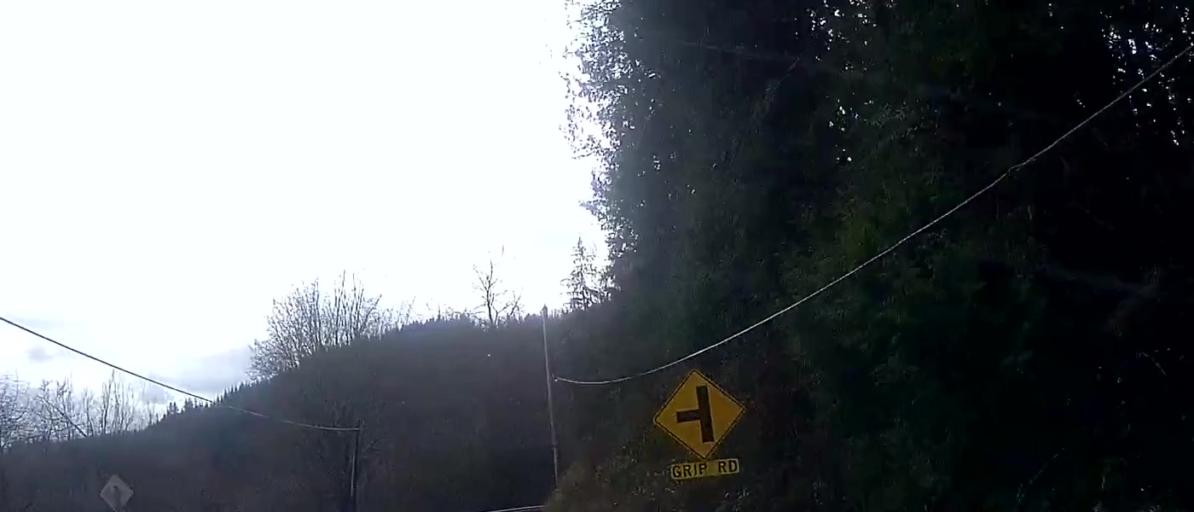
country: US
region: Washington
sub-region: Skagit County
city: Sedro-Woolley
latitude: 48.5570
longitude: -122.2909
